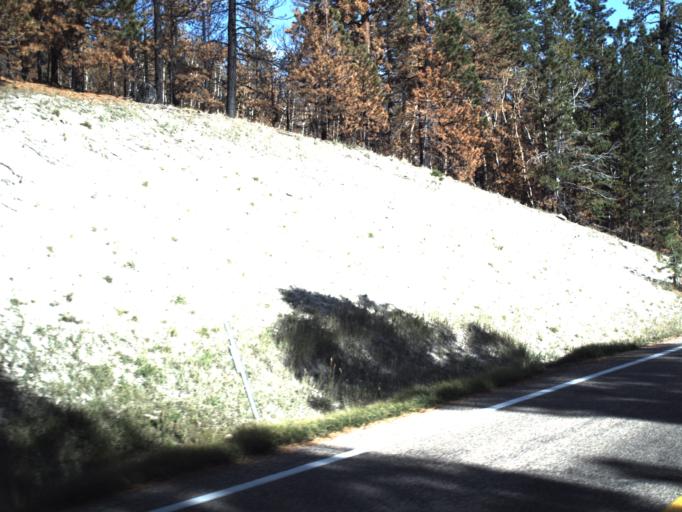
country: US
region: Utah
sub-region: Iron County
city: Parowan
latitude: 37.6532
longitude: -112.7005
